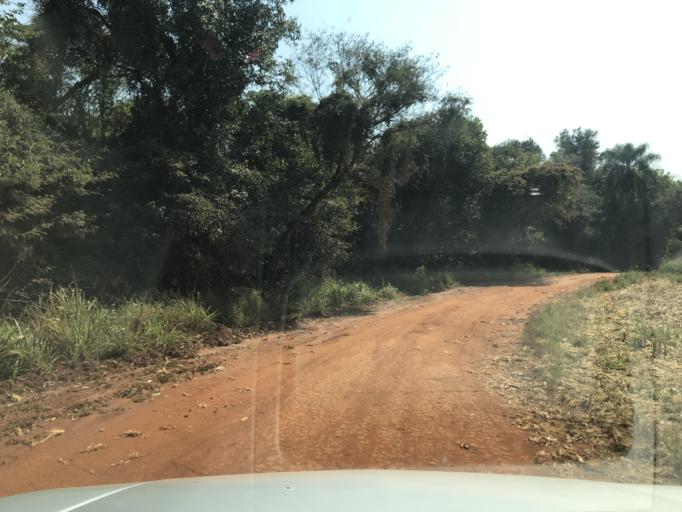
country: BR
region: Parana
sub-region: Palotina
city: Palotina
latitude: -24.2227
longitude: -53.7385
